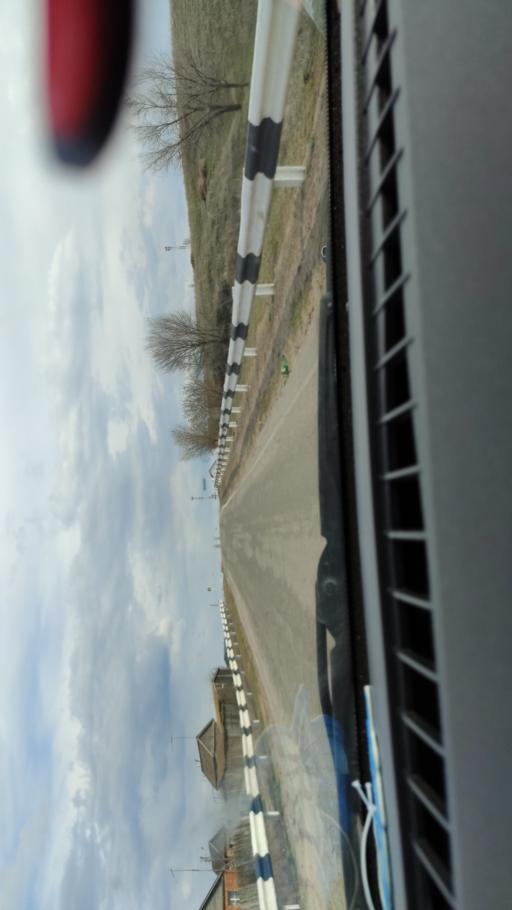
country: RU
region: Saratov
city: Rovnoye
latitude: 51.0258
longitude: 46.0929
